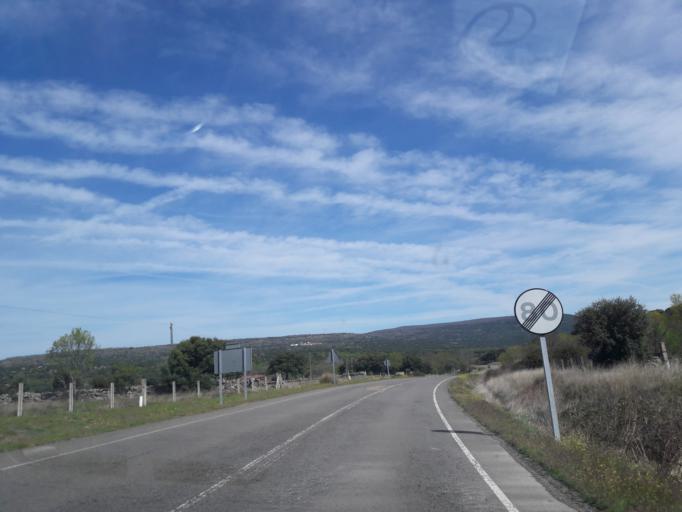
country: ES
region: Castille and Leon
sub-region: Provincia de Salamanca
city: Ledrada
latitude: 40.4762
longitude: -5.7274
